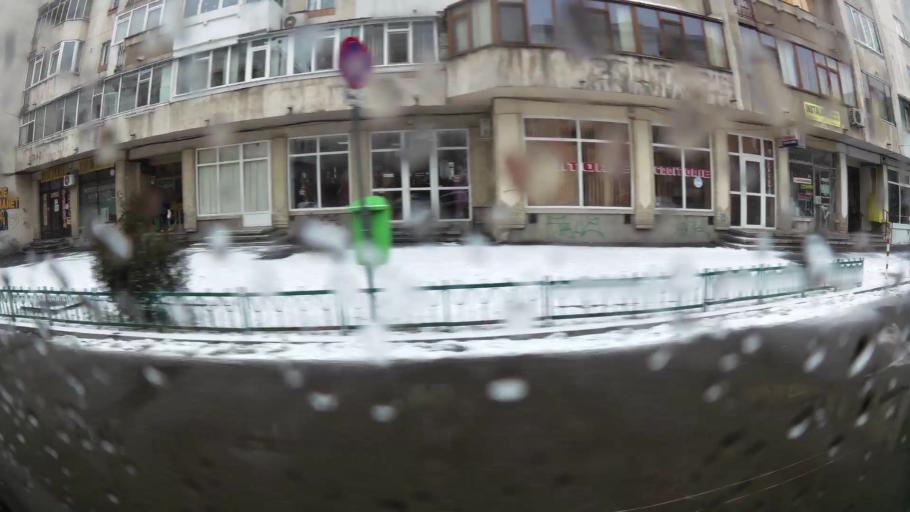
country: RO
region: Prahova
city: Ploiesti
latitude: 44.9405
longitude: 26.0193
